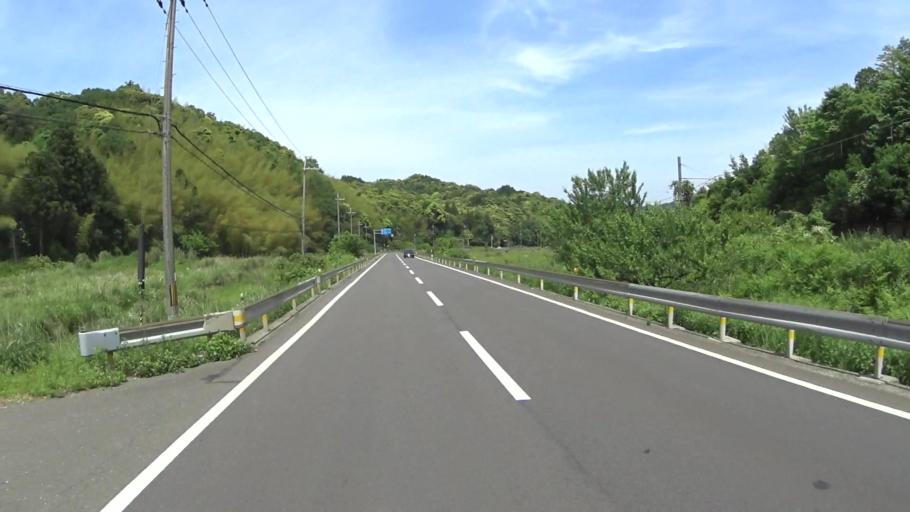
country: JP
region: Fukui
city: Obama
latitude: 35.4824
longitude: 135.6980
